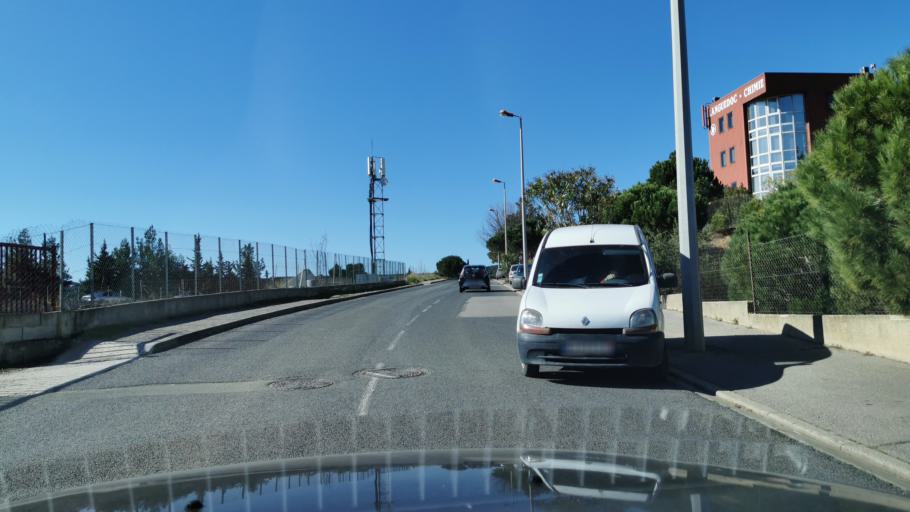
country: FR
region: Languedoc-Roussillon
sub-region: Departement de l'Aude
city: Narbonne
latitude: 43.1527
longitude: 2.9773
